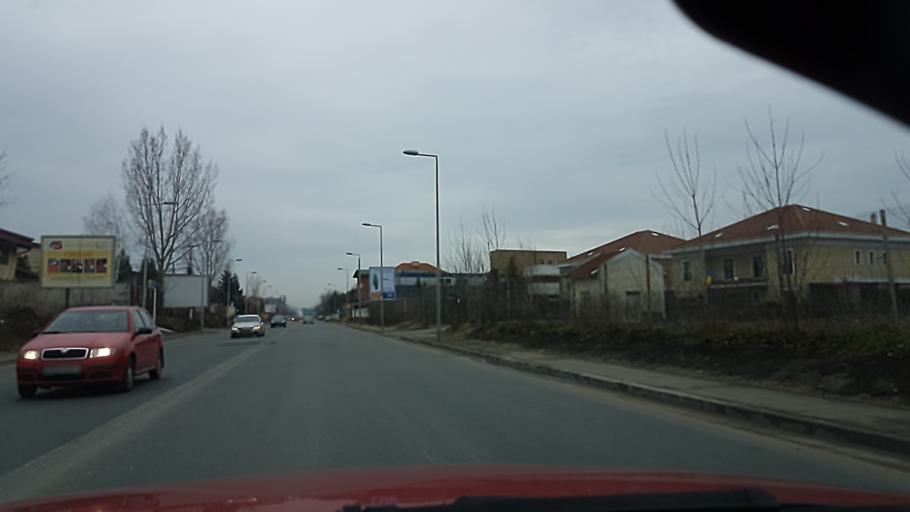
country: RO
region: Ilfov
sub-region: Comuna Tunari
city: Tunari
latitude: 44.5166
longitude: 26.1416
